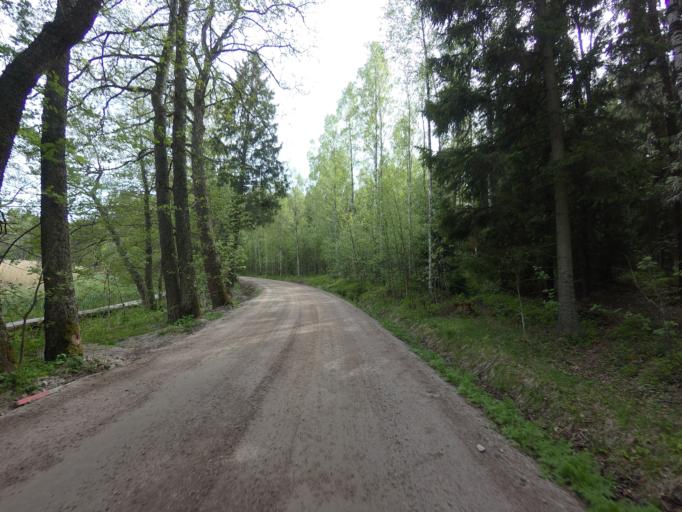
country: FI
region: Uusimaa
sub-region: Helsinki
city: Koukkuniemi
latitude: 60.1340
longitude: 24.6959
